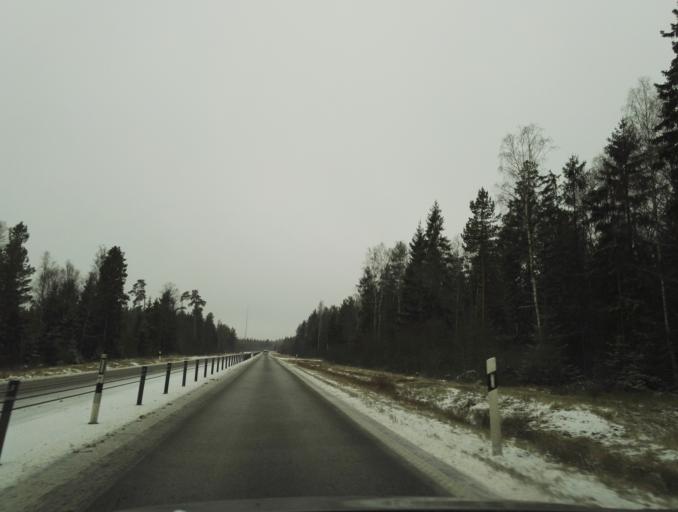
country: SE
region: Kronoberg
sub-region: Alvesta Kommun
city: Vislanda
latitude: 56.7446
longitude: 14.5101
